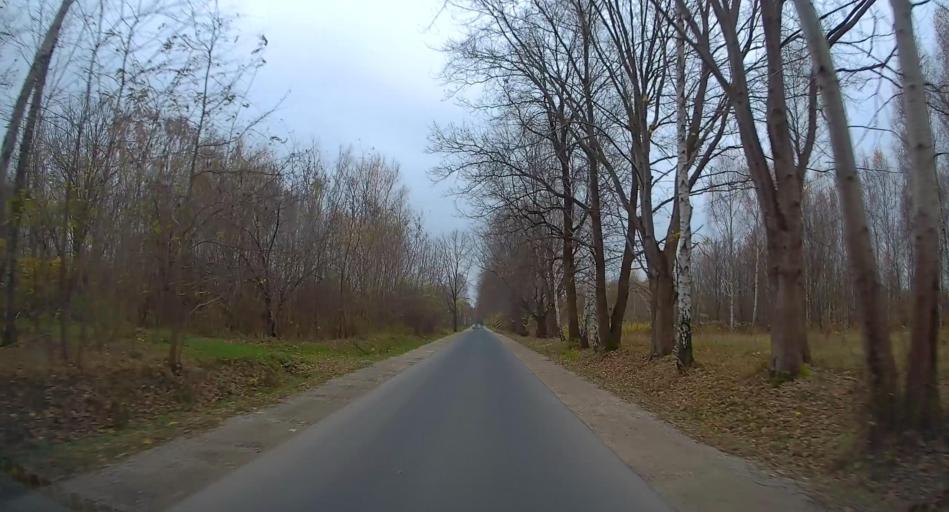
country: PL
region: Lodz Voivodeship
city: Zabia Wola
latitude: 52.0161
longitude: 20.6556
